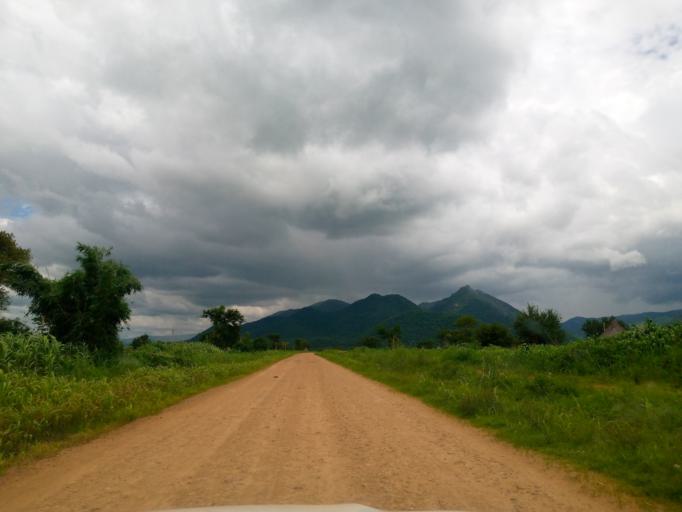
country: ET
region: Oromiya
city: Mendi
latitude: 10.1868
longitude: 35.0931
